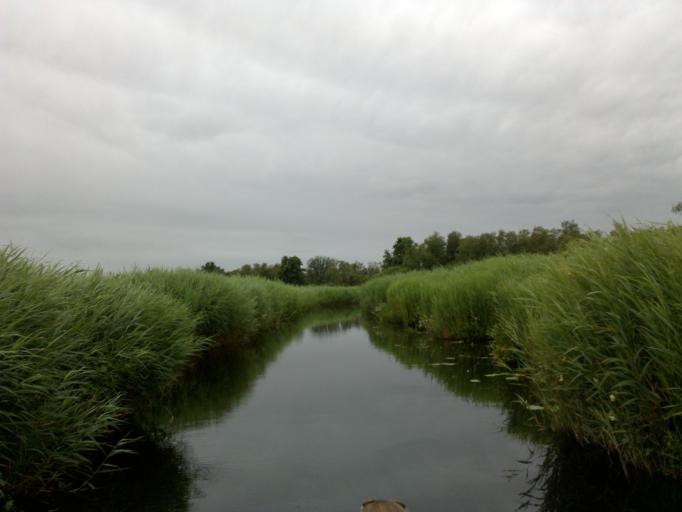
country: NL
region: Overijssel
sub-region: Gemeente Steenwijkerland
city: Sint Jansklooster
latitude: 52.7113
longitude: 6.0367
